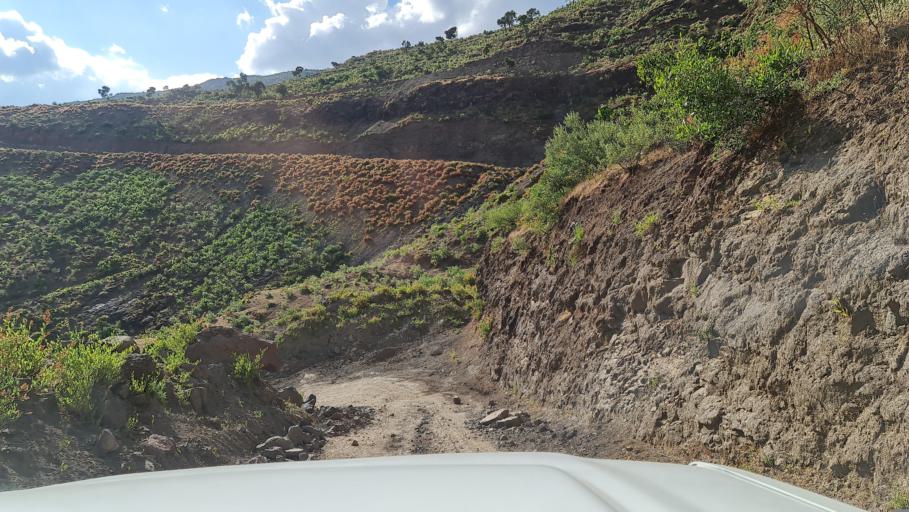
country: ET
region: Amhara
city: Debark'
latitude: 13.1204
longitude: 38.0183
